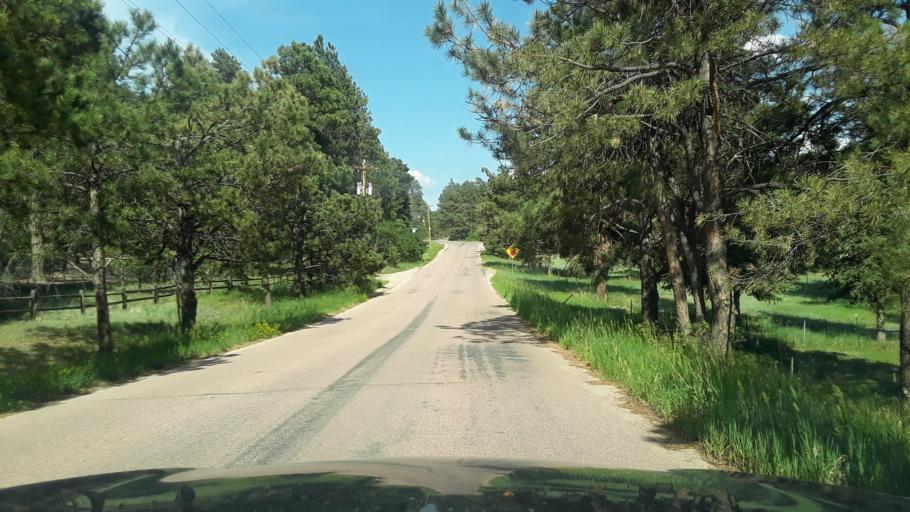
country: US
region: Colorado
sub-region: El Paso County
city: Gleneagle
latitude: 39.0565
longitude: -104.7869
